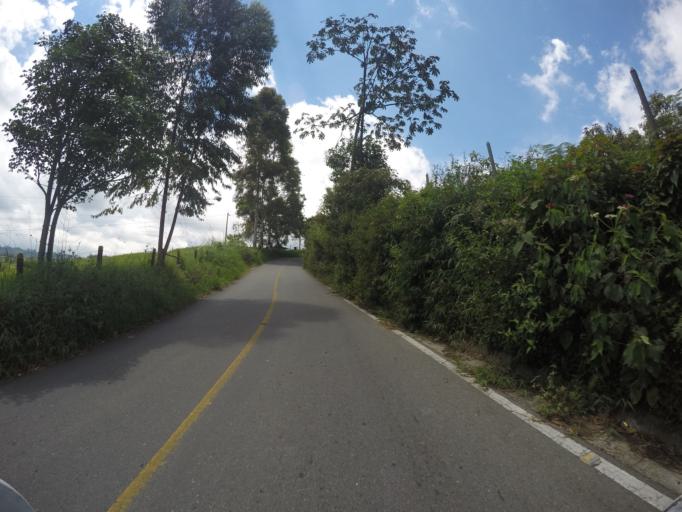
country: CO
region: Quindio
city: Filandia
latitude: 4.6326
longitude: -75.6954
